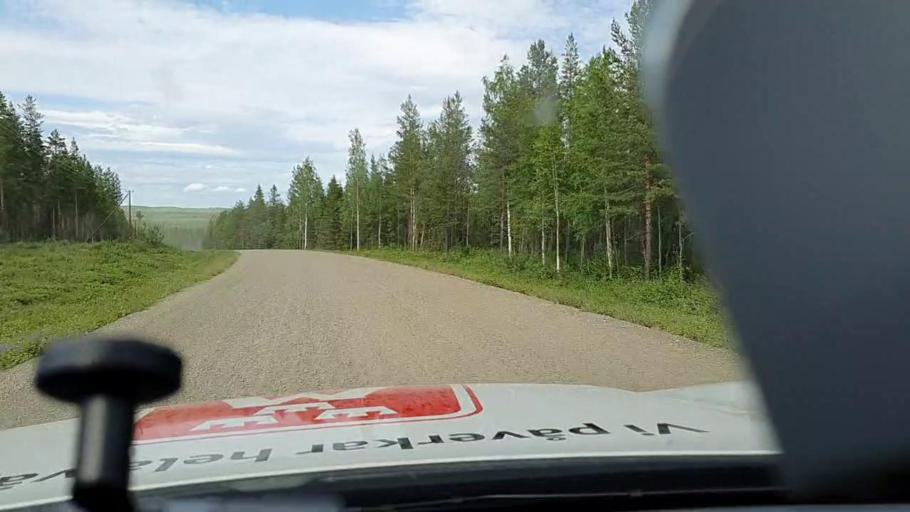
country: SE
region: Norrbotten
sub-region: Alvsbyns Kommun
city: AElvsbyn
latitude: 66.1420
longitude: 21.0165
